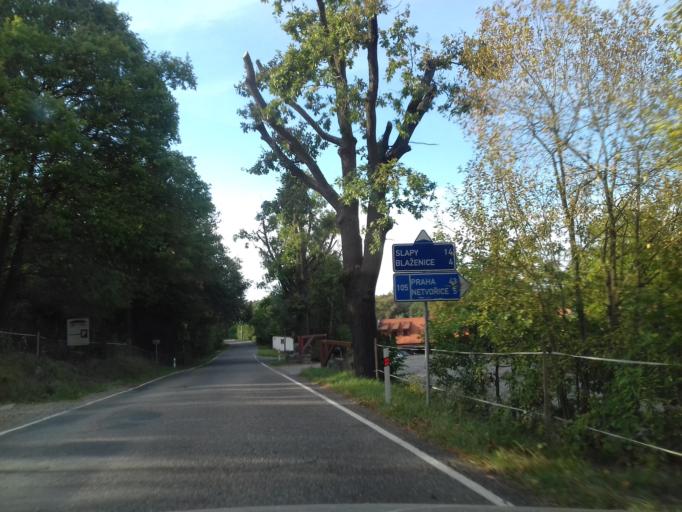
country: CZ
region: Central Bohemia
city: Netvorice
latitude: 49.7883
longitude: 14.5145
